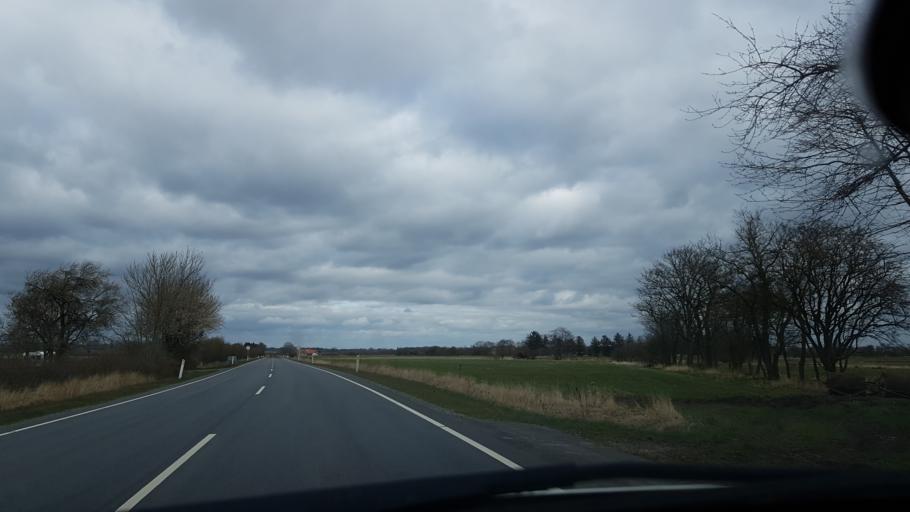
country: DK
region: South Denmark
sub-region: Vejen Kommune
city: Holsted
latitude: 55.4183
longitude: 8.8935
